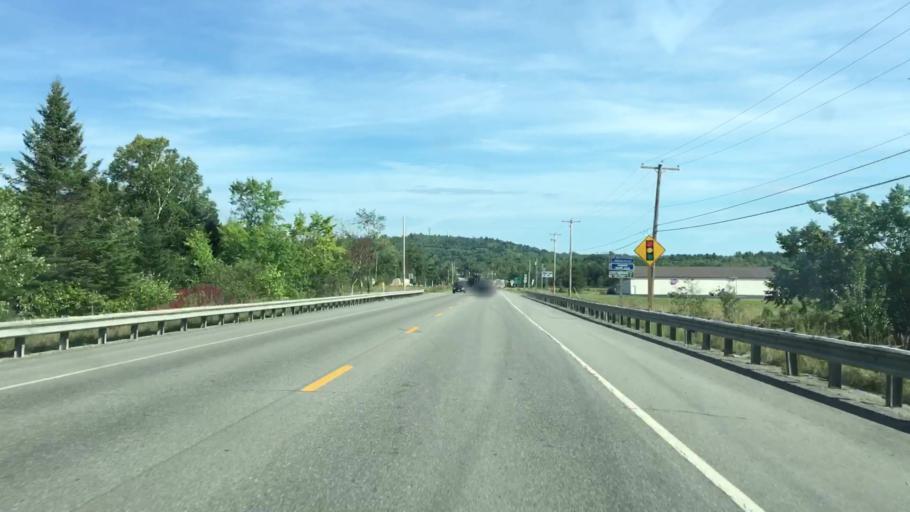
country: US
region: Maine
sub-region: Penobscot County
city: Lincoln
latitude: 45.3556
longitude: -68.5369
